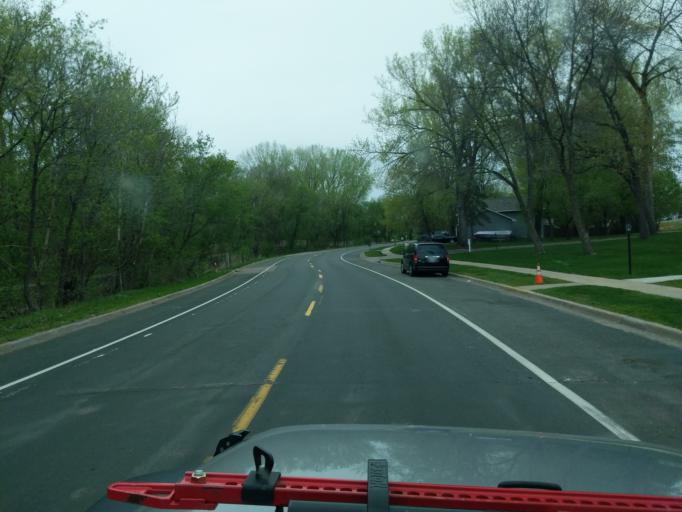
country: US
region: Minnesota
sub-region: Anoka County
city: Coon Rapids
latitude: 45.1519
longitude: -93.3080
